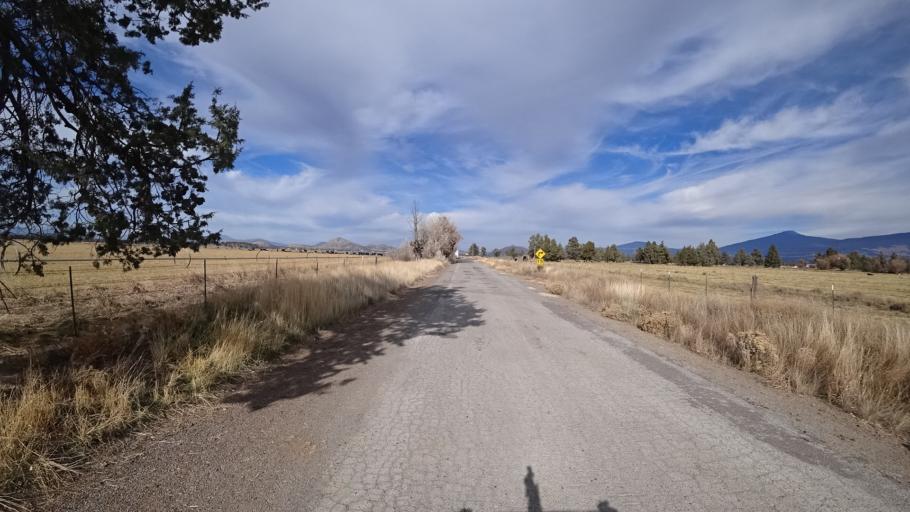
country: US
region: California
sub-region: Siskiyou County
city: Montague
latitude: 41.6080
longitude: -122.4049
